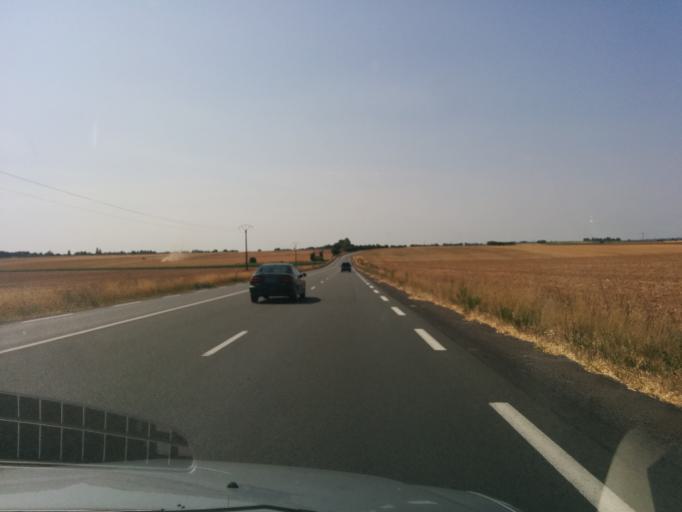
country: FR
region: Poitou-Charentes
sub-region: Departement de la Vienne
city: Neuville-de-Poitou
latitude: 46.6977
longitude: 0.2460
